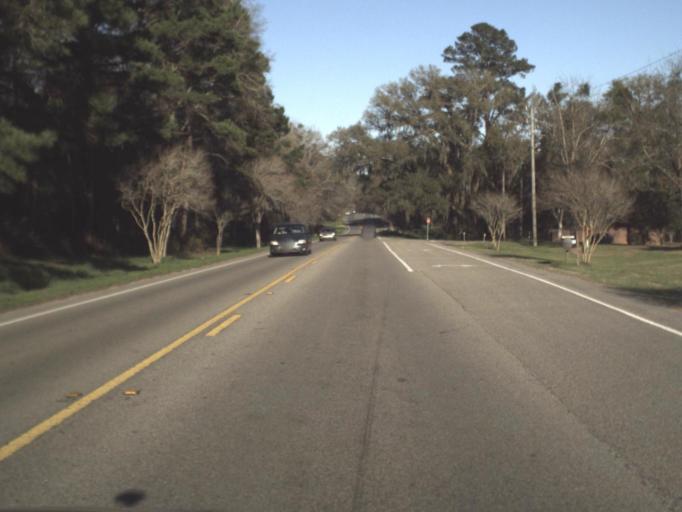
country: US
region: Florida
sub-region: Leon County
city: Tallahassee
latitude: 30.4921
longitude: -84.1209
